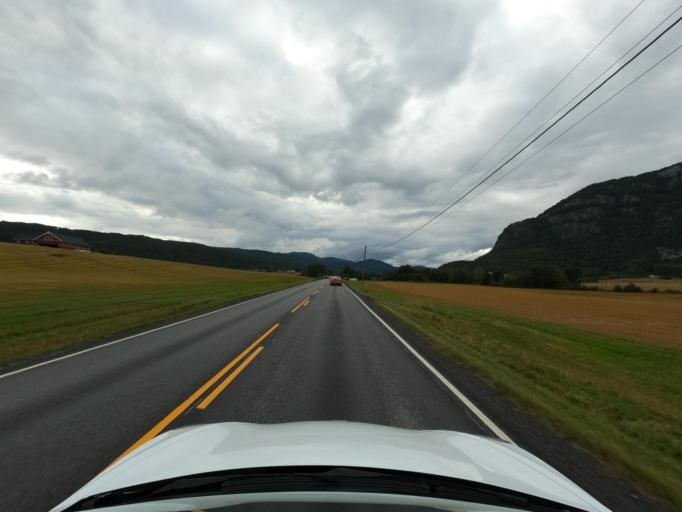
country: NO
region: Telemark
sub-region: Bo
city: Bo
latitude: 59.4072
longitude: 8.9668
